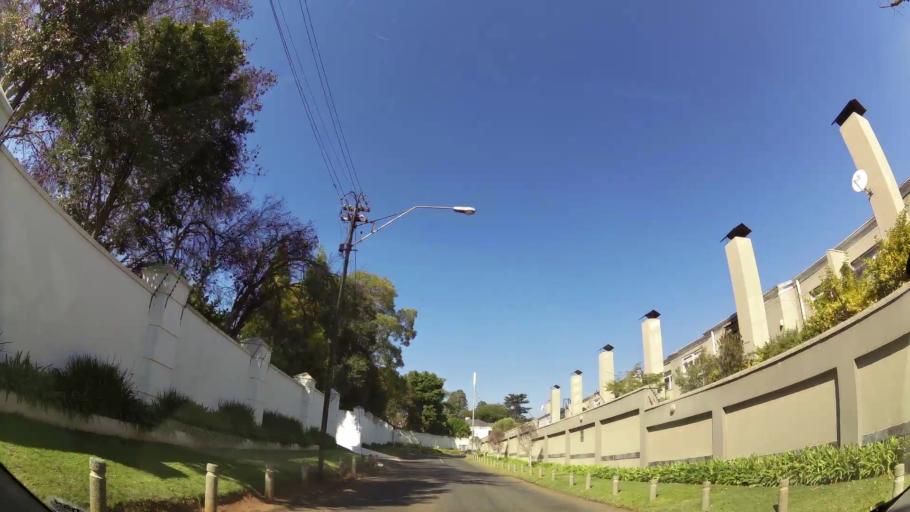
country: ZA
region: Gauteng
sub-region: City of Johannesburg Metropolitan Municipality
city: Johannesburg
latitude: -26.1322
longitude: 28.0393
